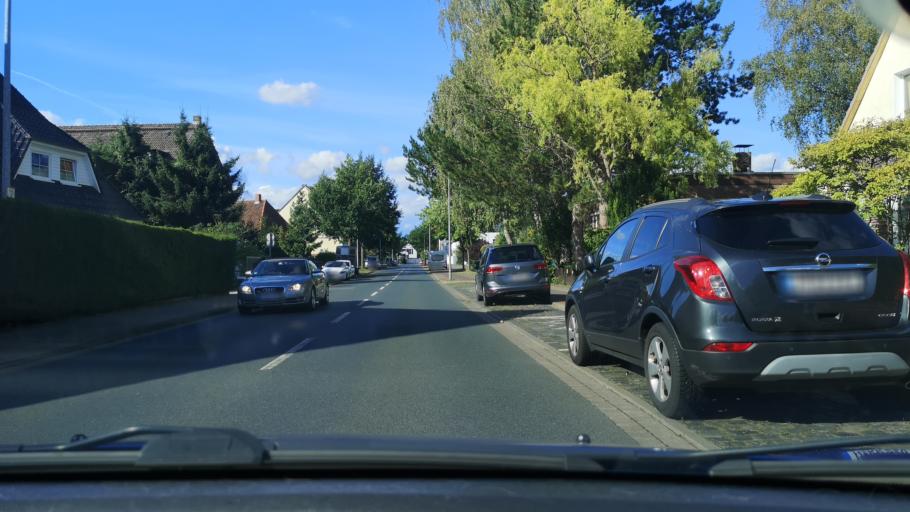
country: DE
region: Lower Saxony
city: Isernhagen Farster Bauerschaft
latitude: 52.4153
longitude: 9.8067
